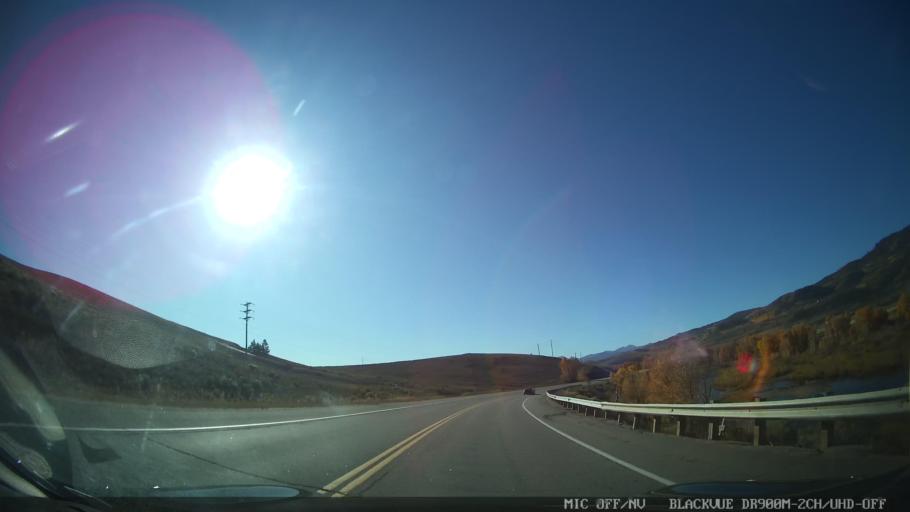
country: US
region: Colorado
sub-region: Grand County
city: Granby
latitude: 40.1068
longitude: -105.9752
